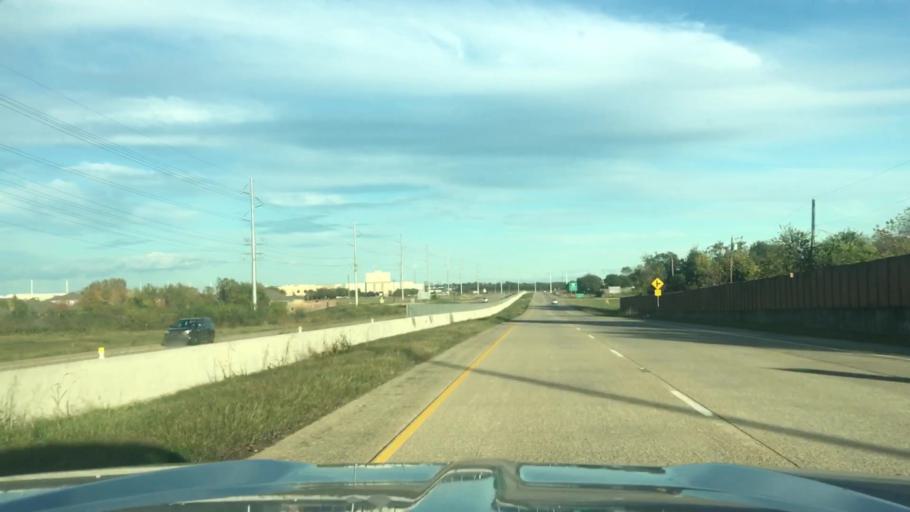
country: US
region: Texas
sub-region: Denton County
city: Denton
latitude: 33.2602
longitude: -97.1254
